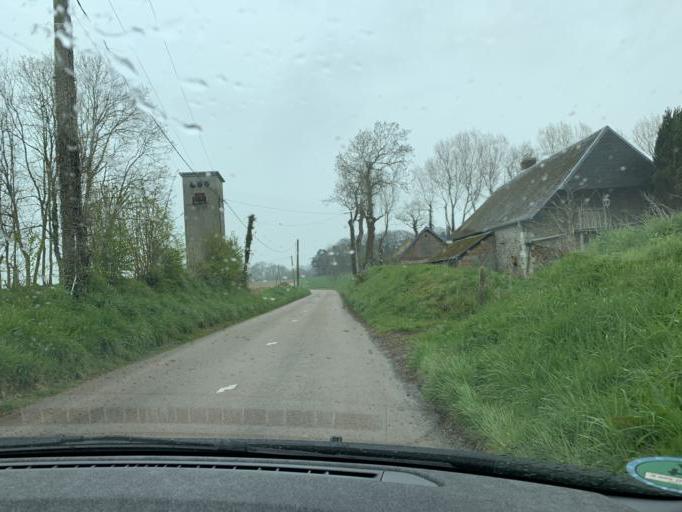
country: FR
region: Haute-Normandie
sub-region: Departement de la Seine-Maritime
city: Les Loges
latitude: 49.7186
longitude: 0.2643
